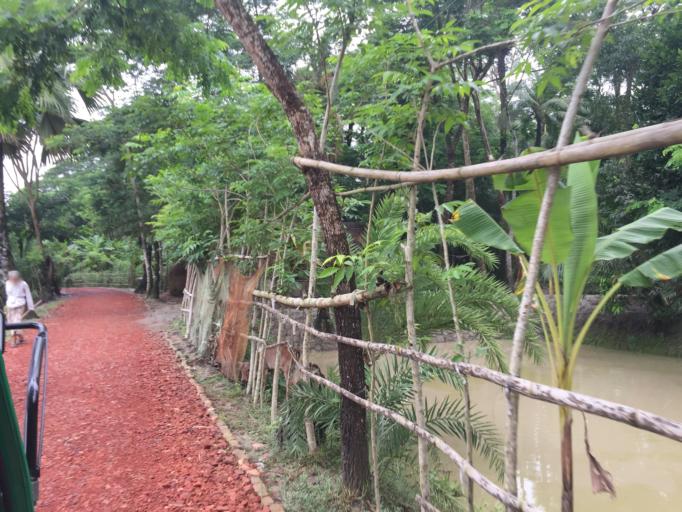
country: BD
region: Barisal
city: Mathba
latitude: 22.1981
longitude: 89.9347
